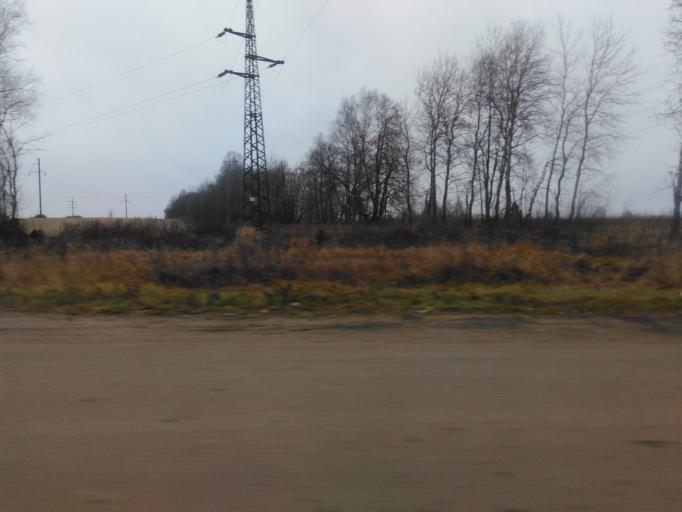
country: RU
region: Moskovskaya
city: Ashukino
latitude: 56.1323
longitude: 37.9776
